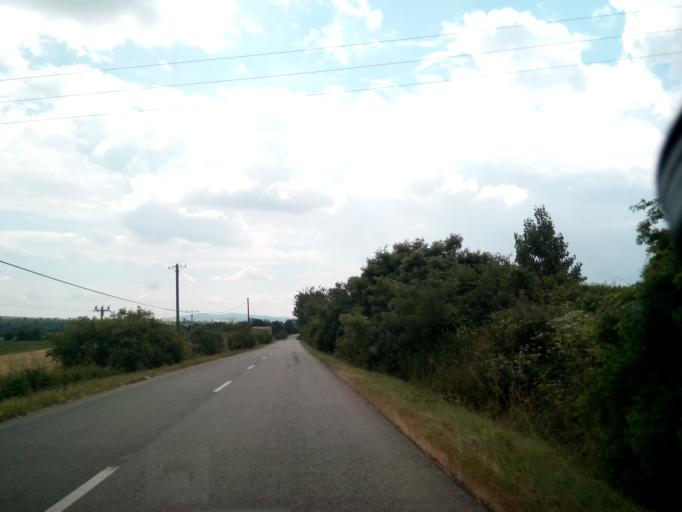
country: SK
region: Kosicky
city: Secovce
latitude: 48.5917
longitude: 21.5628
